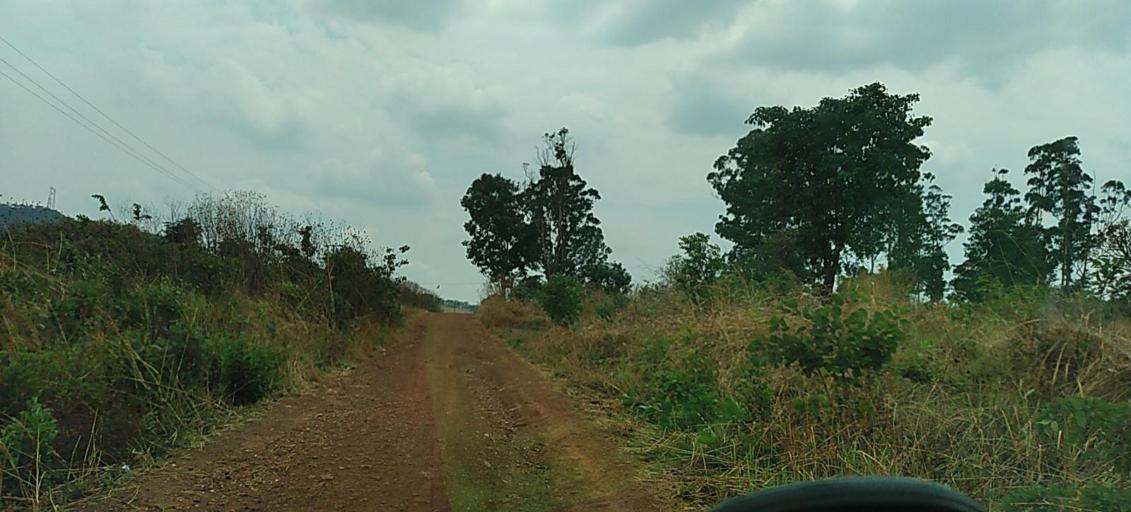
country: ZM
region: North-Western
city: Kansanshi
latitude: -12.0320
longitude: 26.4353
